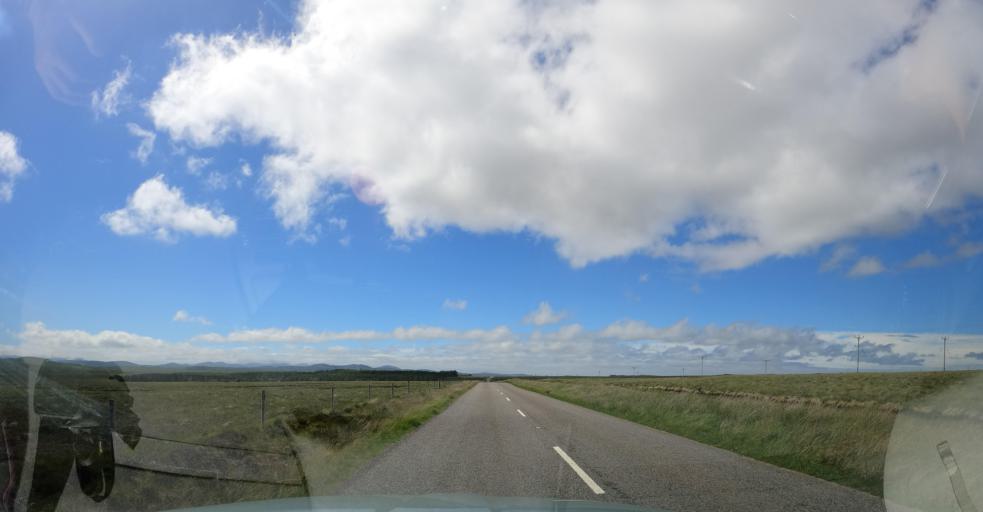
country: GB
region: Scotland
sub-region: Eilean Siar
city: Isle of Lewis
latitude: 58.1781
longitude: -6.6332
